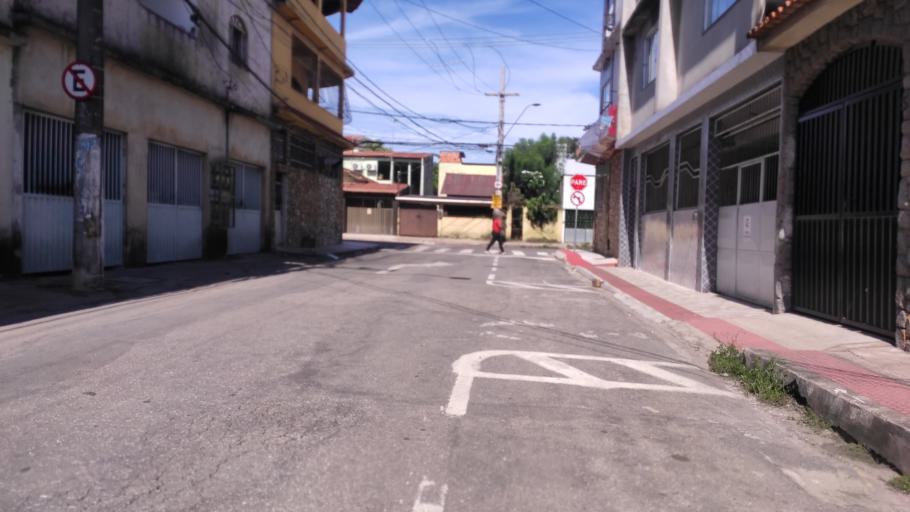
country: BR
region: Espirito Santo
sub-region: Serra
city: Serra
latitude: -20.1943
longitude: -40.2706
